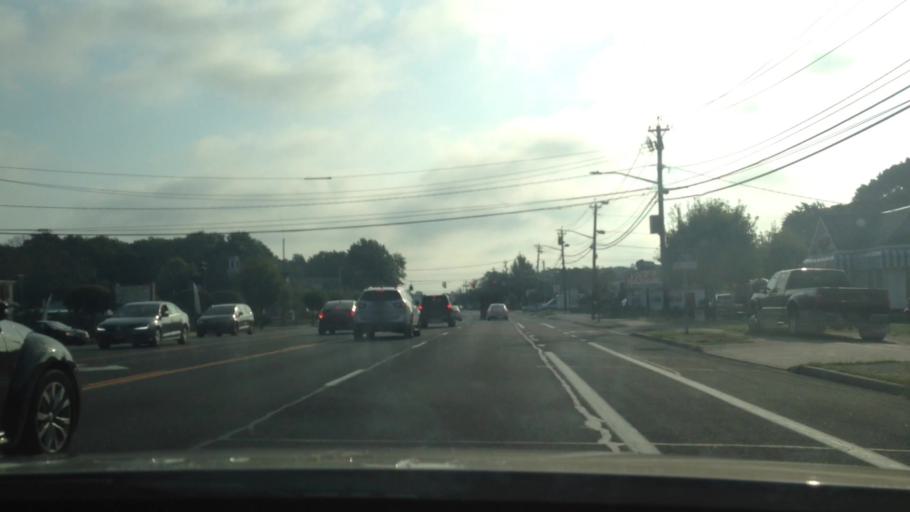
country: US
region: New York
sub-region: Suffolk County
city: Selden
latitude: 40.8618
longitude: -73.0611
